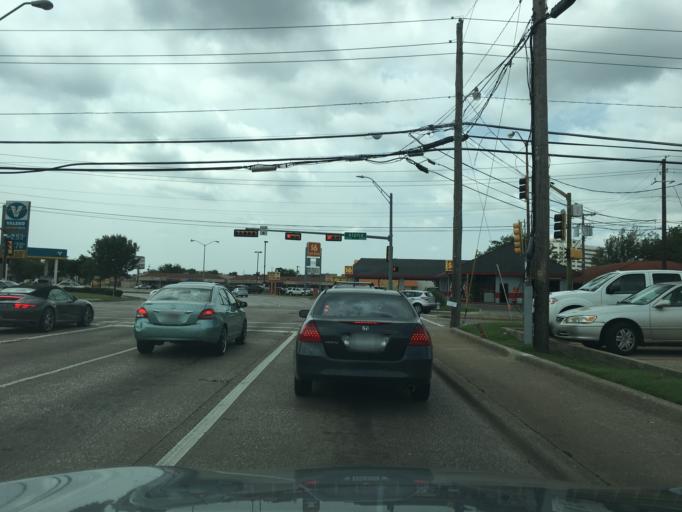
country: US
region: Texas
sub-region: Dallas County
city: Addison
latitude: 32.9338
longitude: -96.8134
